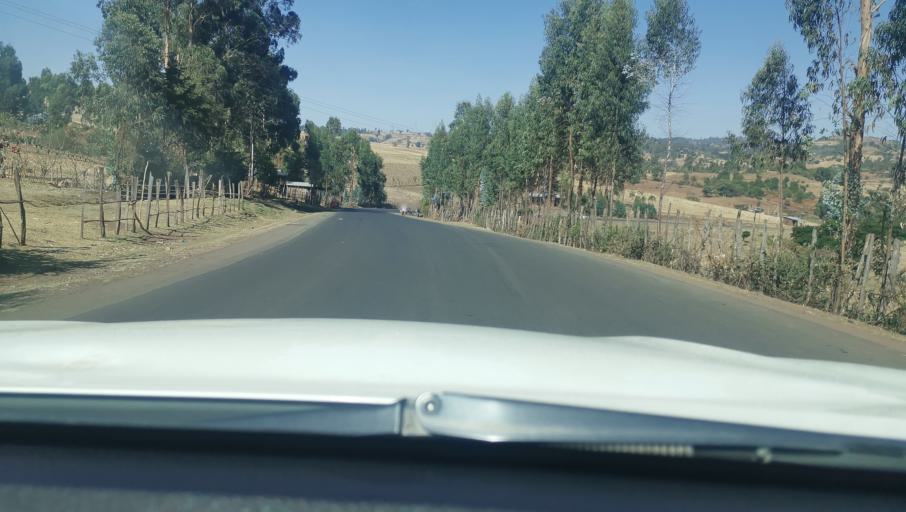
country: ET
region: Oromiya
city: Gedo
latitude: 8.9685
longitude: 37.5210
